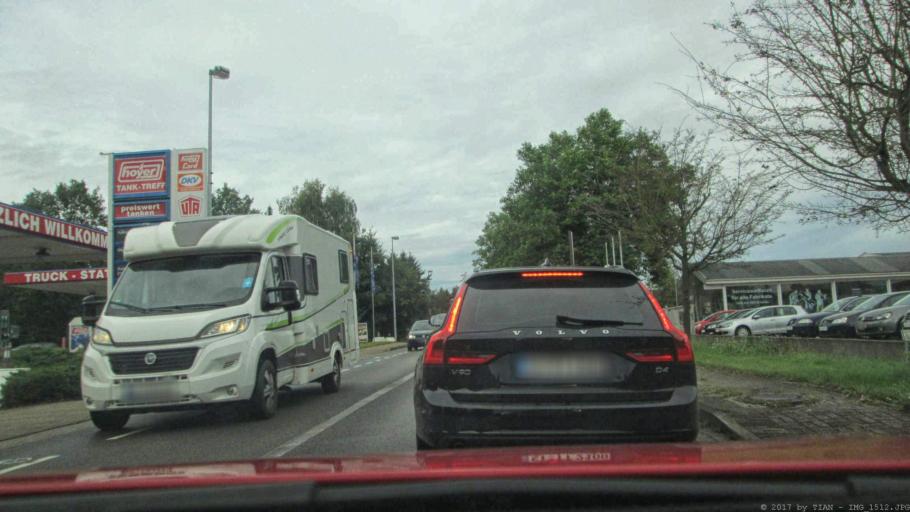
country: DE
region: Lower Saxony
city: Bodenteich
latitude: 52.8403
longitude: 10.6822
